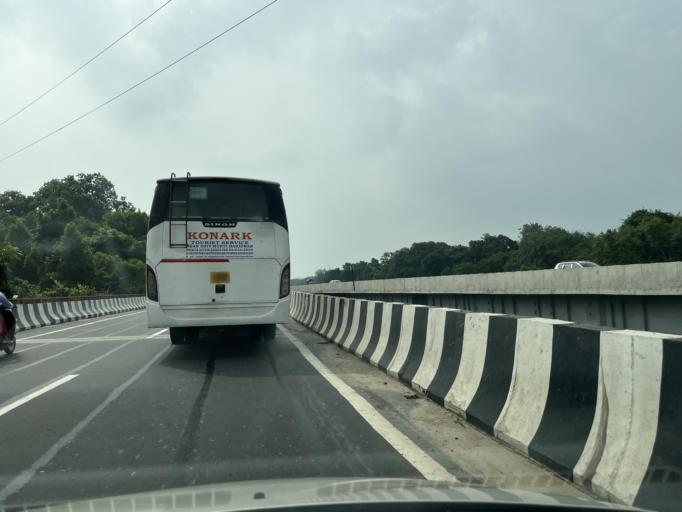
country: IN
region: Uttarakhand
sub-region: Dehradun
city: Raiwala
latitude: 30.0684
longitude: 78.2074
